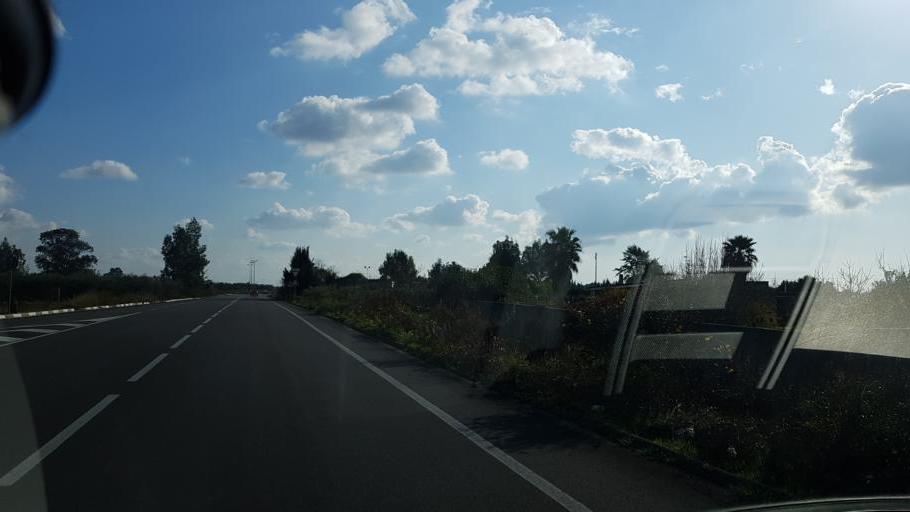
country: IT
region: Apulia
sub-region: Provincia di Lecce
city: Veglie
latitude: 40.3410
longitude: 17.9787
